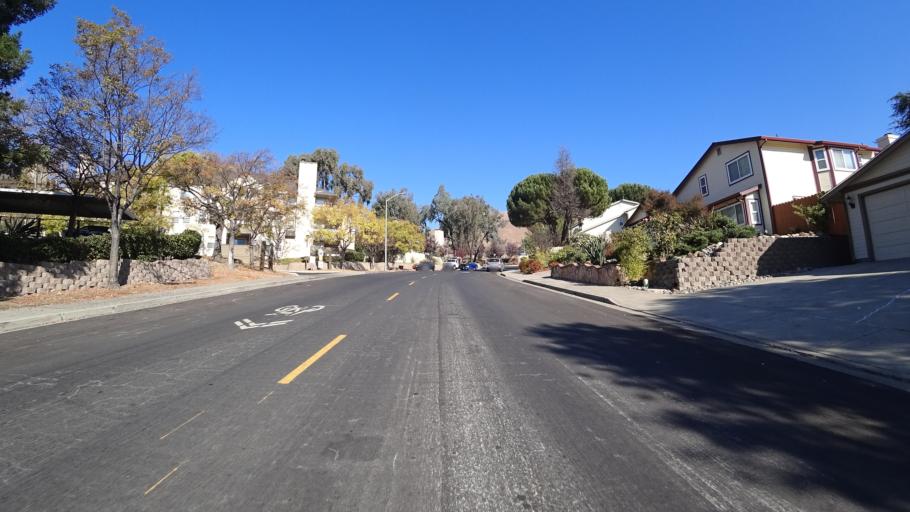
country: US
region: California
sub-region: Alameda County
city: Union City
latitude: 37.6321
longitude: -122.0445
